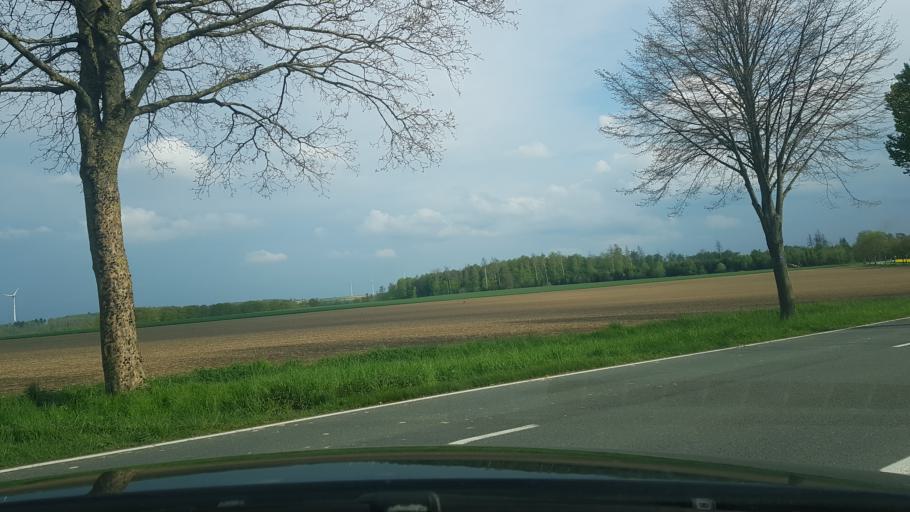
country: DE
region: North Rhine-Westphalia
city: Lichtenau
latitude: 51.6340
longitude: 8.8302
